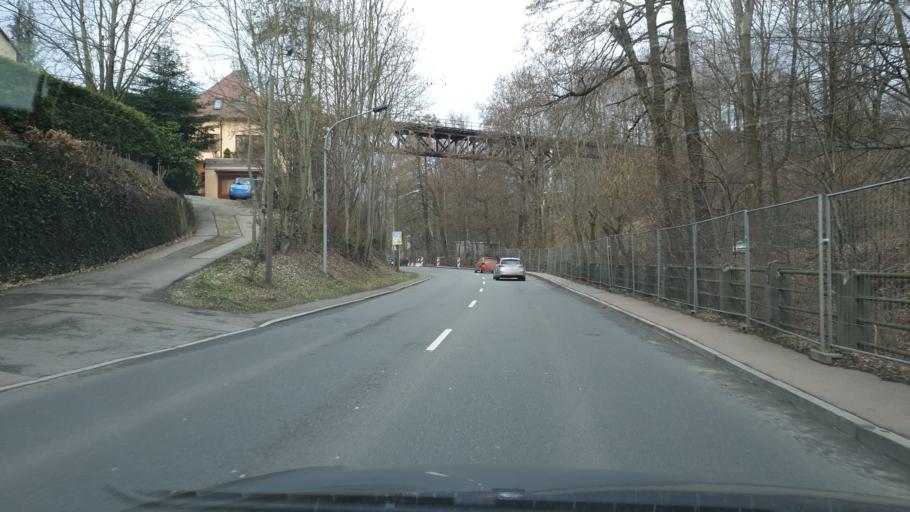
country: DE
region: Saxony
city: Mittweida
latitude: 50.9786
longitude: 12.9747
